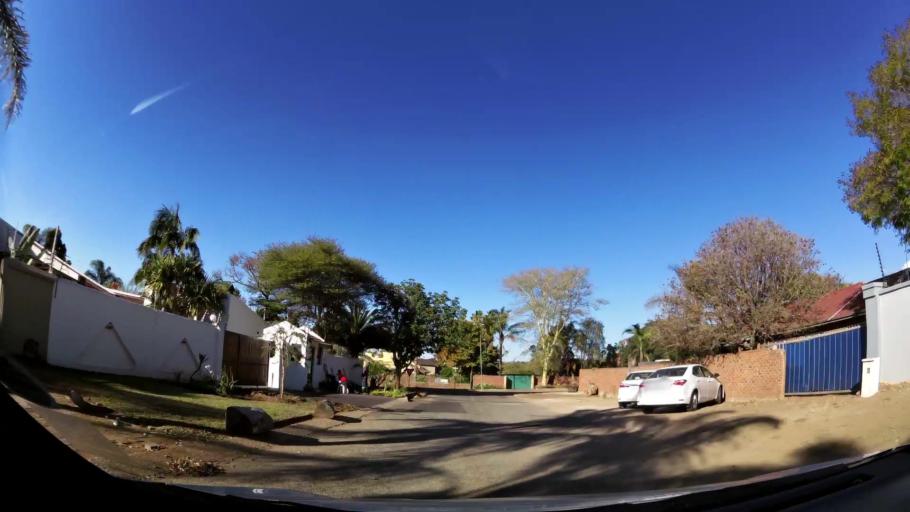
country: ZA
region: Limpopo
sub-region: Capricorn District Municipality
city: Polokwane
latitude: -23.8836
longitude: 29.4898
